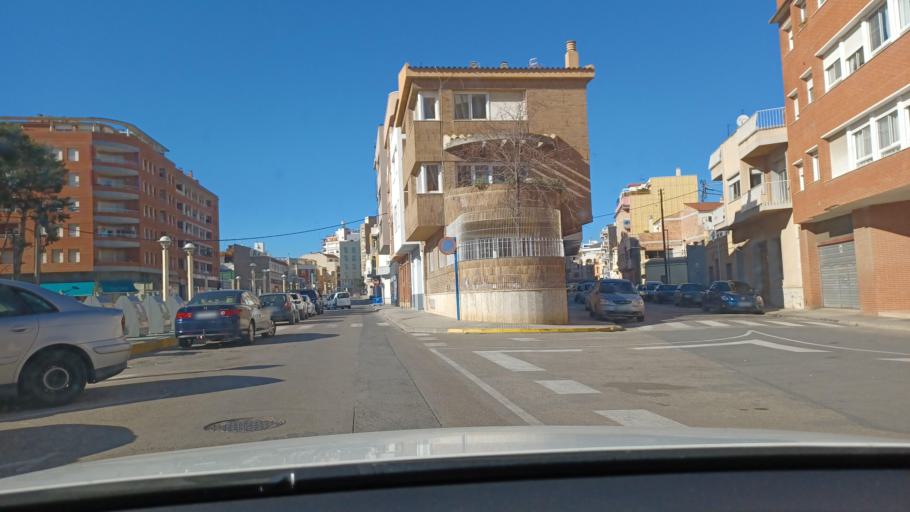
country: ES
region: Catalonia
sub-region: Provincia de Tarragona
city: Amposta
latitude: 40.7108
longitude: 0.5827
